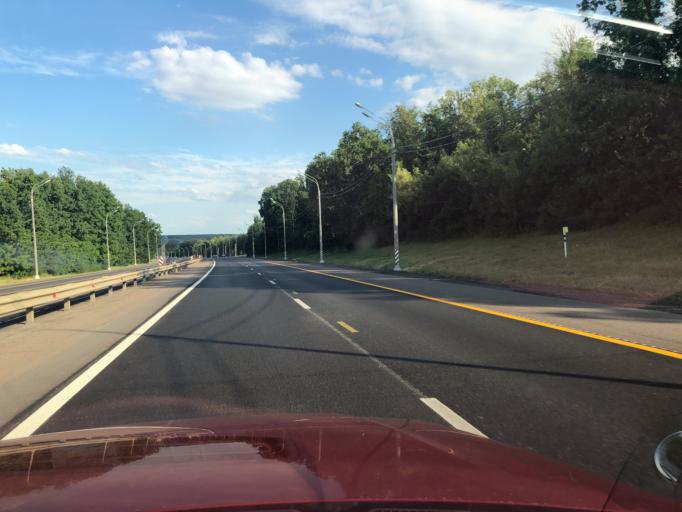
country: RU
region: Lipetsk
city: Zadonsk
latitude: 52.3850
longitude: 38.8696
